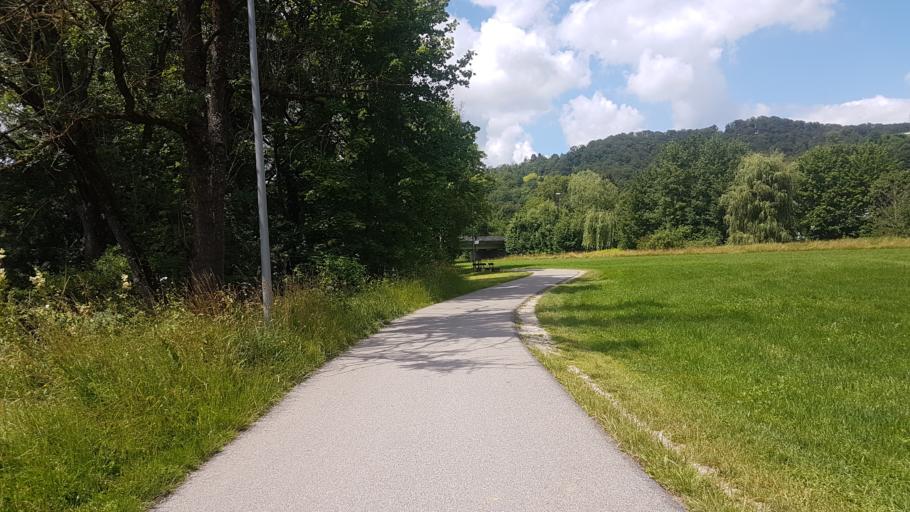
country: DE
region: Bavaria
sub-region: Upper Bavaria
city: Eichstaett
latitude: 48.8991
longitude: 11.1682
